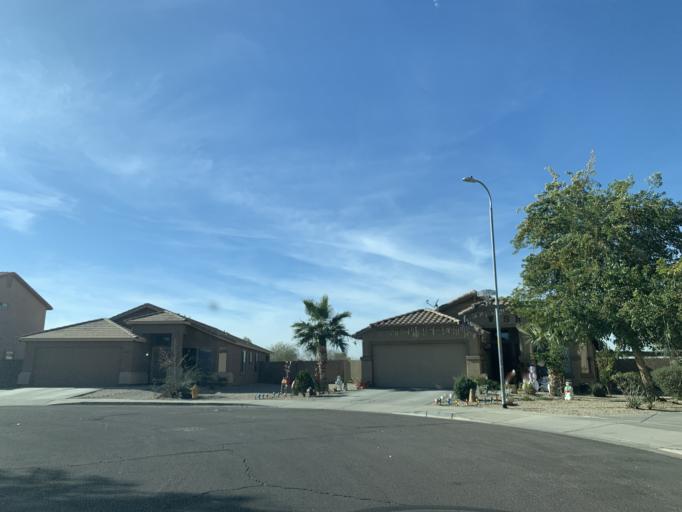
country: US
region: Arizona
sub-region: Maricopa County
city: Laveen
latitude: 33.3896
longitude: -112.1395
